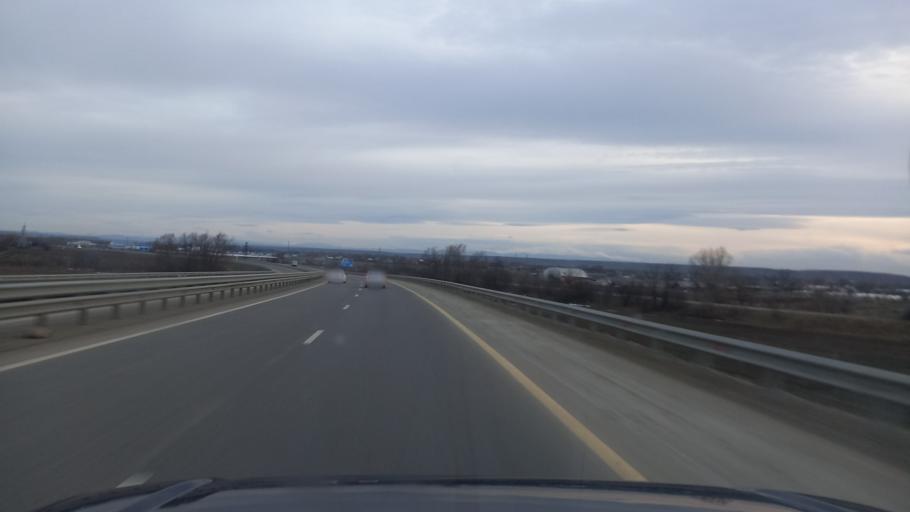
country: RU
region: Adygeya
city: Khanskaya
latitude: 44.6972
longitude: 39.9690
